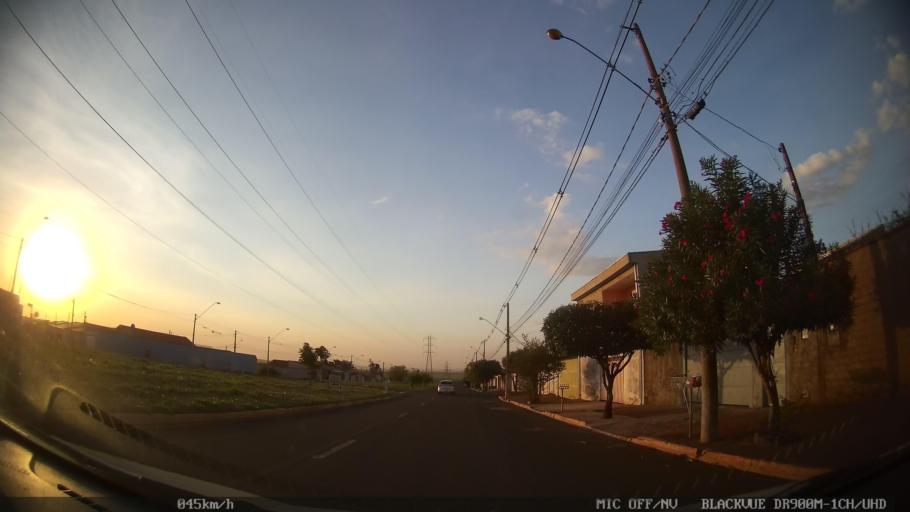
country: BR
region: Sao Paulo
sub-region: Ribeirao Preto
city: Ribeirao Preto
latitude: -21.1406
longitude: -47.8573
